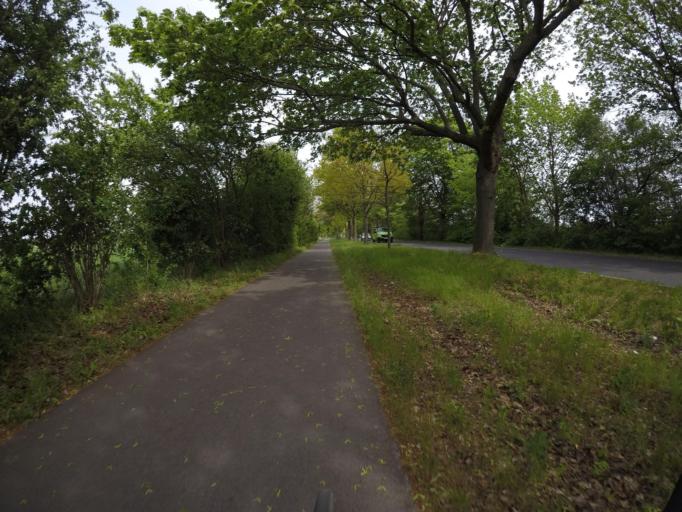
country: DE
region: Berlin
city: Gropiusstadt
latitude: 52.4070
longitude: 13.4683
